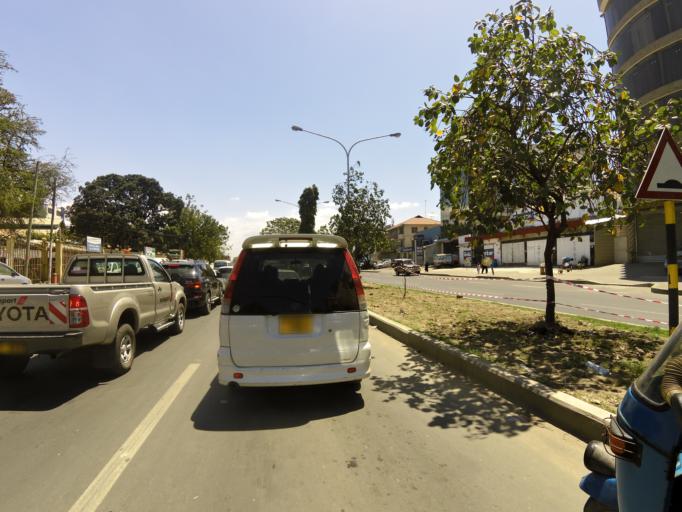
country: TZ
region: Dar es Salaam
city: Dar es Salaam
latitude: -6.8265
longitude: 39.2781
